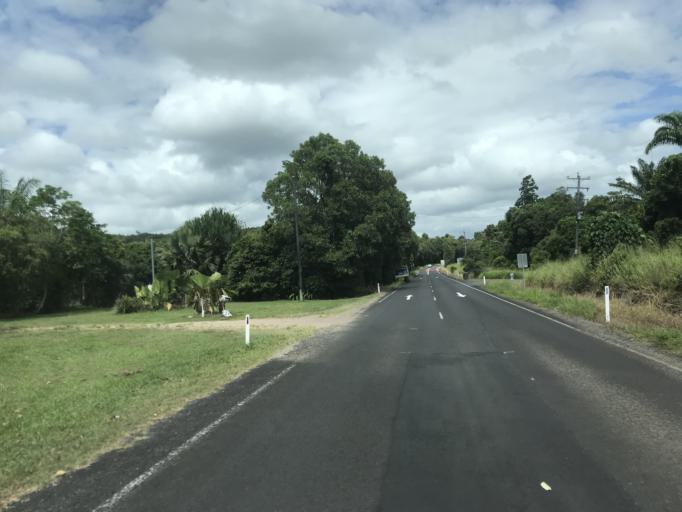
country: AU
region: Queensland
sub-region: Cassowary Coast
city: Innisfail
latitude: -17.8702
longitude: 146.0884
